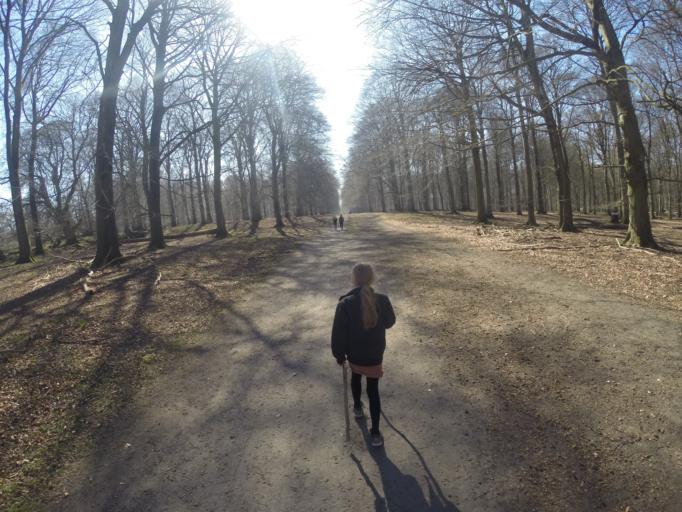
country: DK
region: Capital Region
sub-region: Gentofte Kommune
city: Charlottenlund
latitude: 55.7846
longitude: 12.5571
